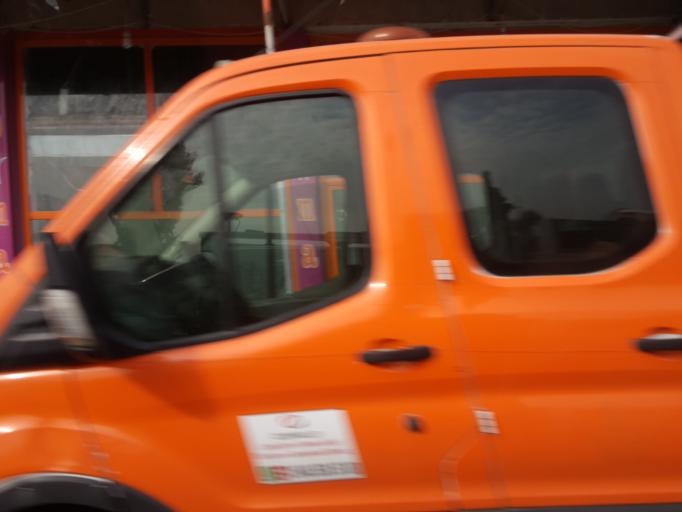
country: TR
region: Kirikkale
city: Bahsili
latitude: 39.8148
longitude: 33.4722
